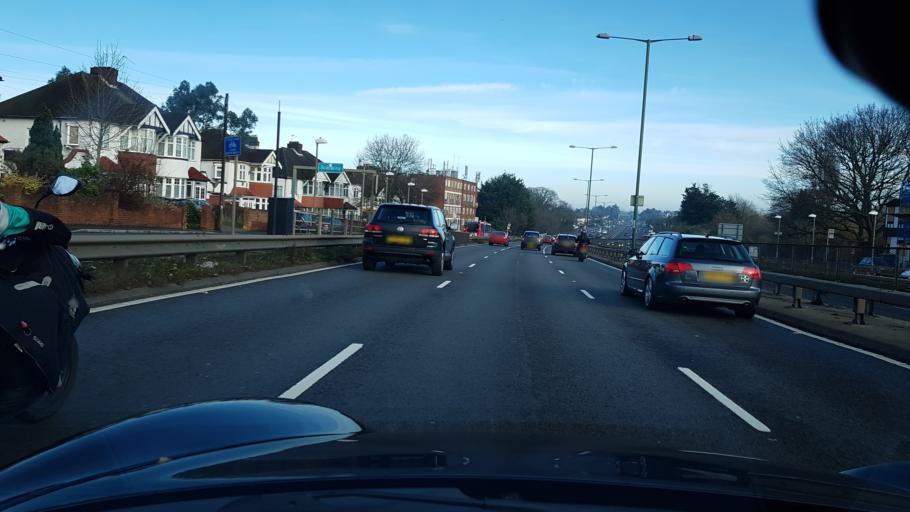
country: GB
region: England
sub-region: Greater London
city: New Malden
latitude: 51.3871
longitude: -0.2725
